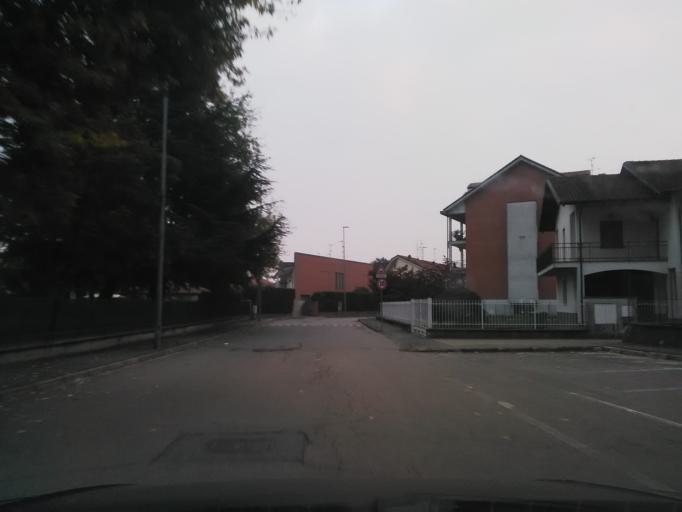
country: IT
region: Piedmont
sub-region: Provincia di Vercelli
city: Santhia
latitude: 45.3685
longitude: 8.1760
